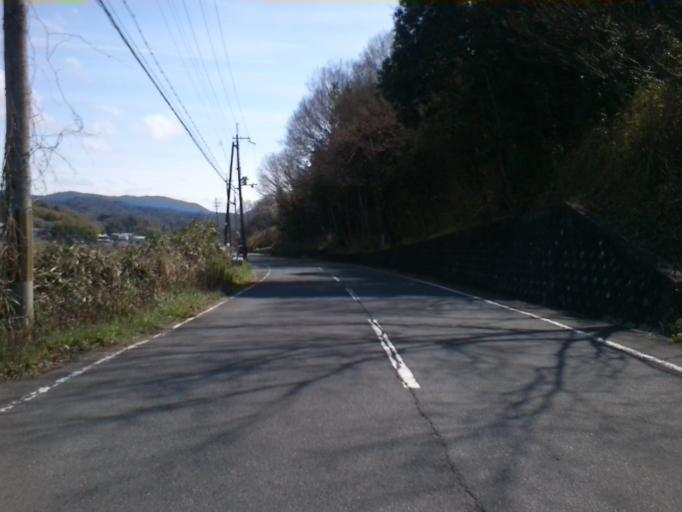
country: JP
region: Nara
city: Nara-shi
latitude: 34.7281
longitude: 135.8640
